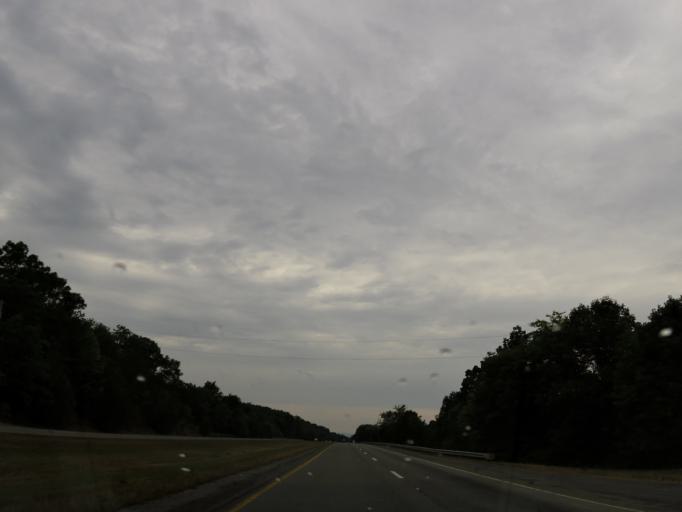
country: US
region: Alabama
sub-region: Jackson County
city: Scottsboro
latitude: 34.6215
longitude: -86.2034
